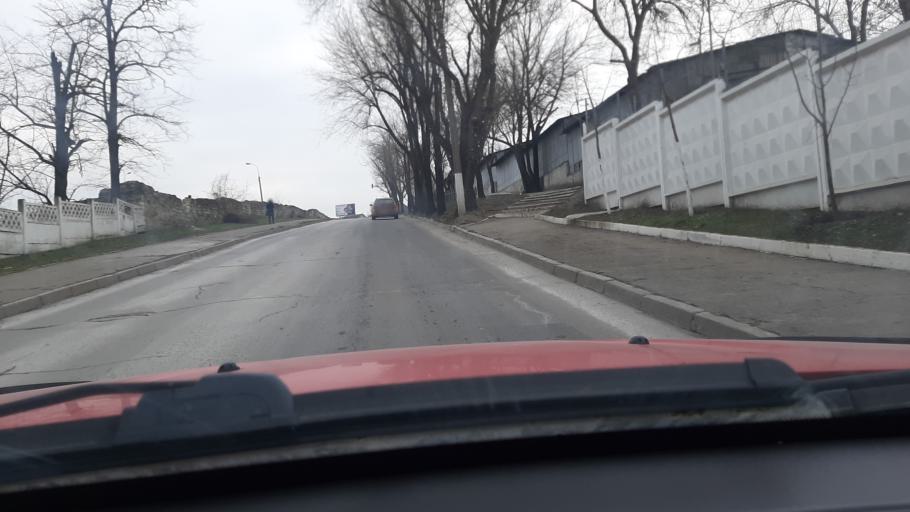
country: MD
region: Chisinau
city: Vatra
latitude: 47.0365
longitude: 28.7950
